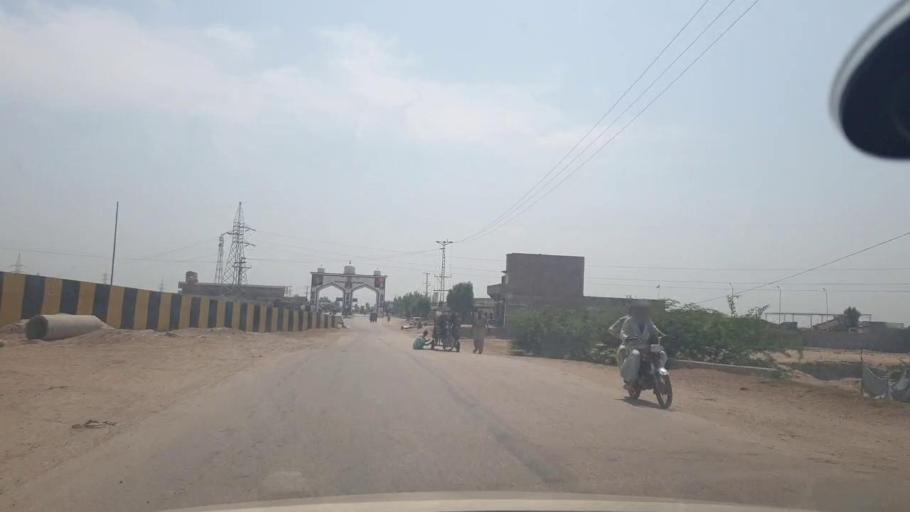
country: PK
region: Sindh
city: Jacobabad
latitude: 28.2439
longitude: 68.4674
